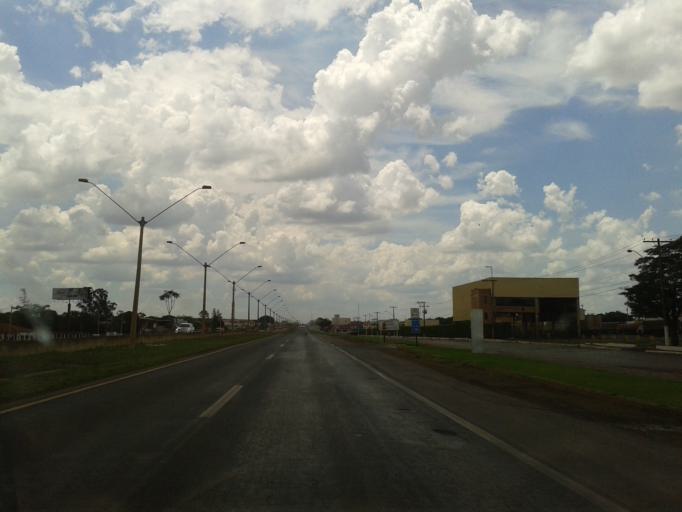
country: BR
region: Goias
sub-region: Itumbiara
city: Itumbiara
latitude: -18.3871
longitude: -49.2071
